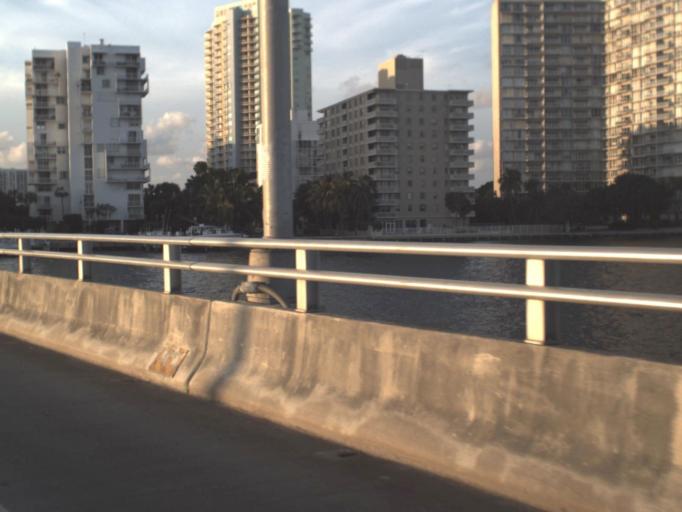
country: US
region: Florida
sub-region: Miami-Dade County
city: Miami
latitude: 25.7473
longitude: -80.2005
